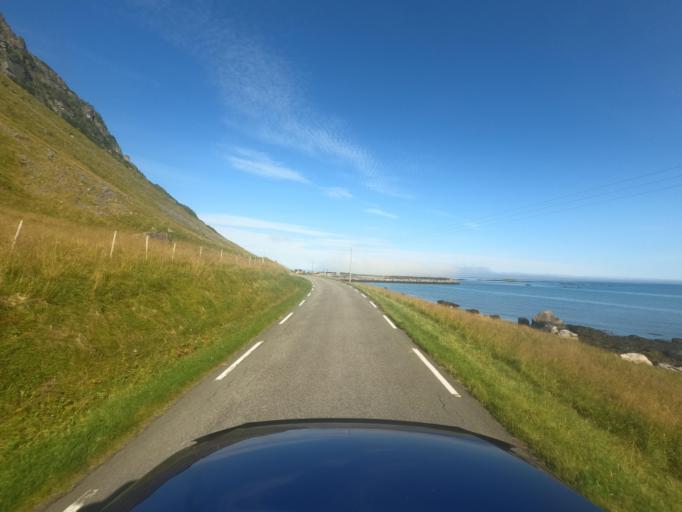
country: NO
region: Nordland
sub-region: Vestvagoy
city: Evjen
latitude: 68.3288
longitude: 13.9981
